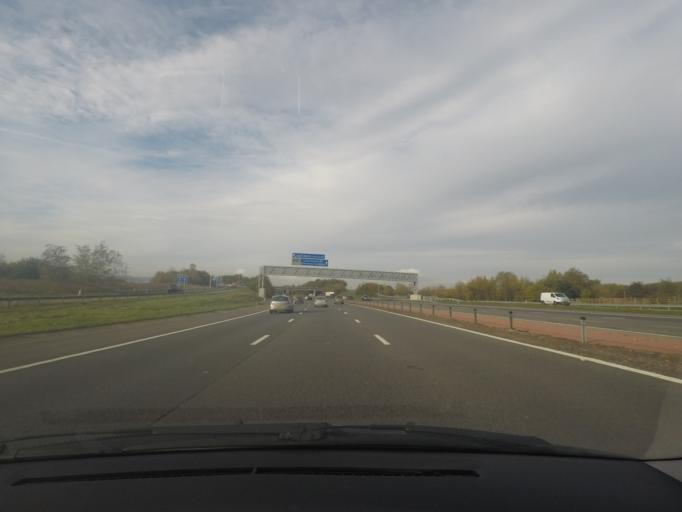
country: GB
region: England
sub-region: City and Borough of Leeds
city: Swillington
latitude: 53.7769
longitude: -1.4649
